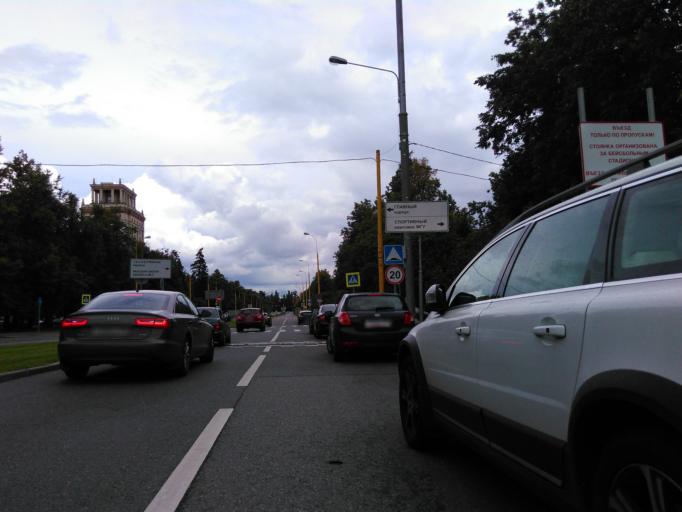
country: RU
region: Moscow
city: Vorob'yovo
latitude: 55.7000
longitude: 37.5320
